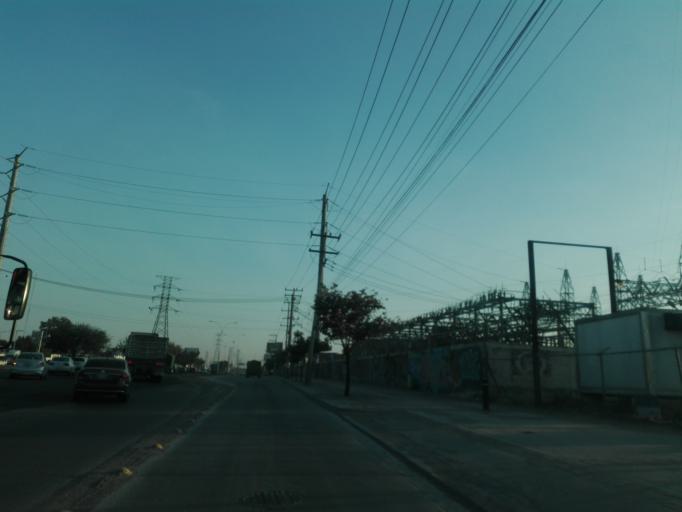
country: MX
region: Guanajuato
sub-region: Leon
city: Medina
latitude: 21.1365
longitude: -101.6317
